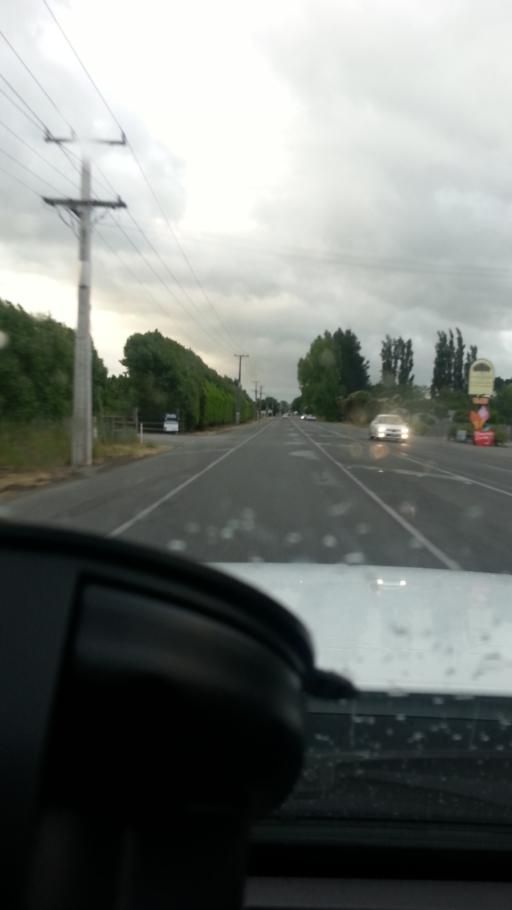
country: NZ
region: Wellington
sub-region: Masterton District
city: Masterton
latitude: -41.0707
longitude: 175.4712
